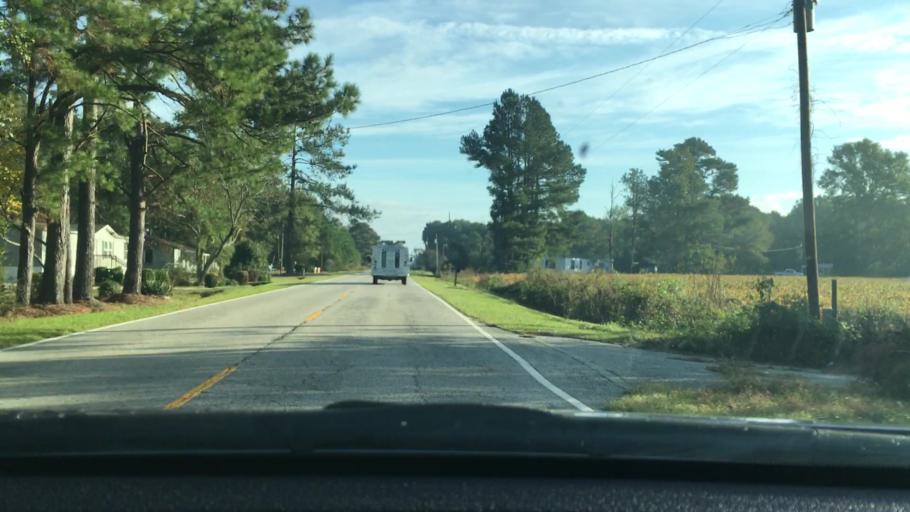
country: US
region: South Carolina
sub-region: Sumter County
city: East Sumter
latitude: 34.0456
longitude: -80.2550
